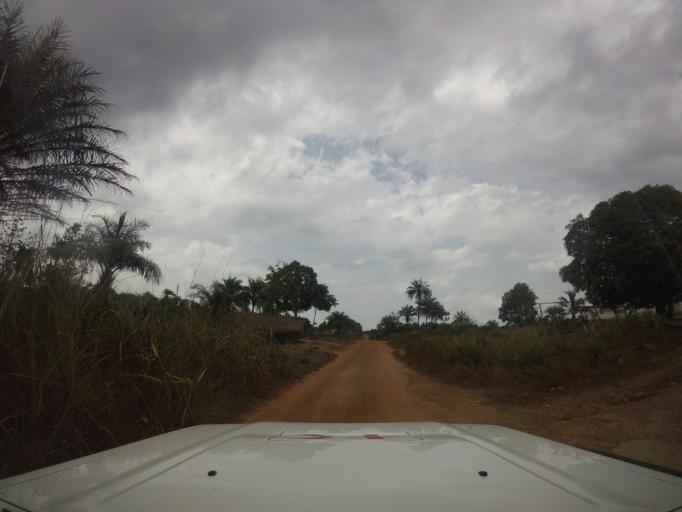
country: LR
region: Grand Cape Mount
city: Robertsport
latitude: 6.9633
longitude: -11.3159
